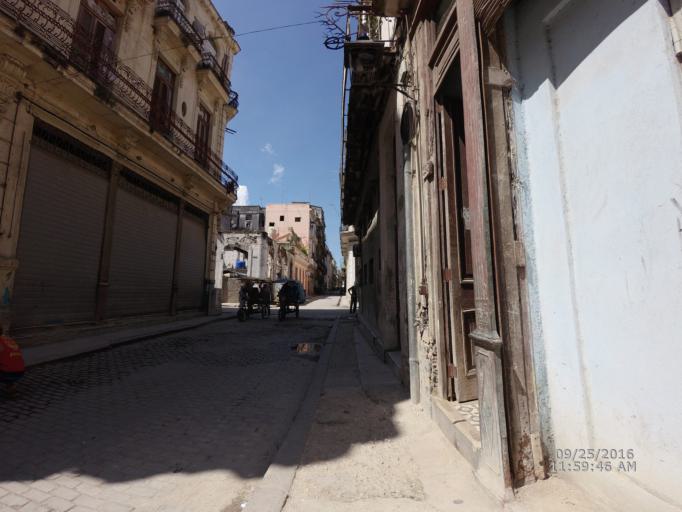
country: CU
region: La Habana
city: La Habana Vieja
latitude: 23.1382
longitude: -82.3529
